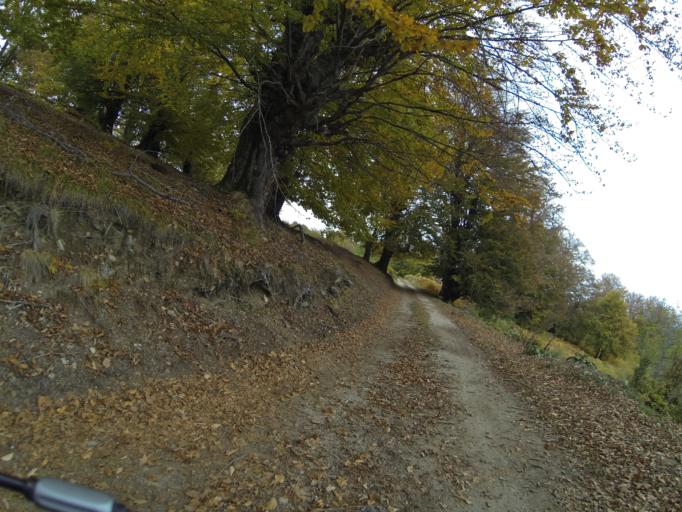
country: RO
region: Gorj
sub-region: Comuna Tismana
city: Sohodol
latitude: 45.1284
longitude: 22.8662
